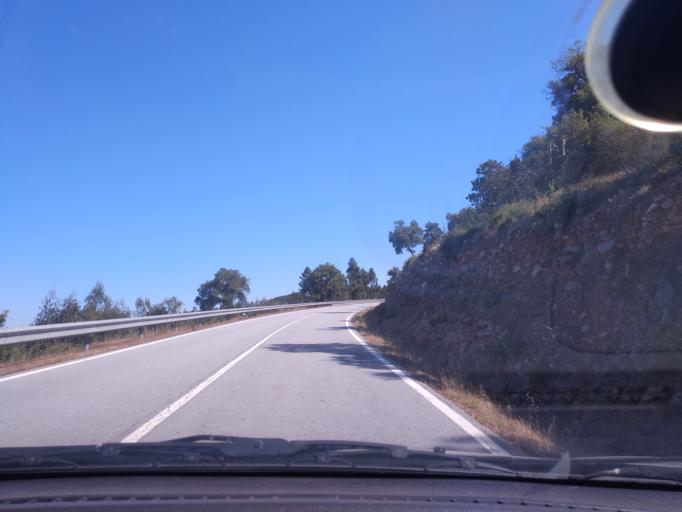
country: PT
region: Portalegre
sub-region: Nisa
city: Nisa
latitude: 39.5989
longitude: -7.6624
